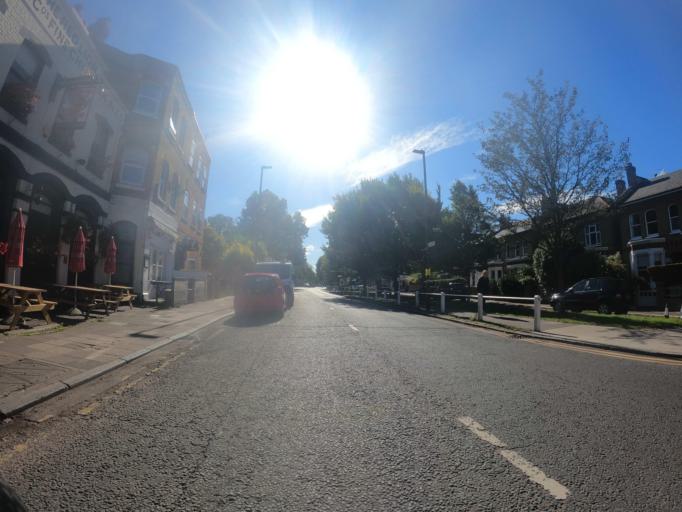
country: GB
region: England
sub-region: Greater London
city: Ealing
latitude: 51.5083
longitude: -0.3052
